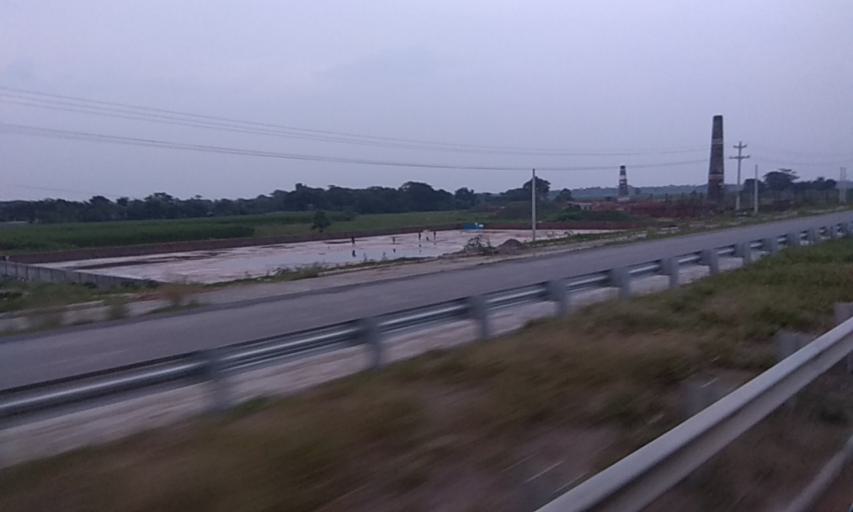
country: BD
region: Dhaka
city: Char Bhadrasan
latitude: 23.3704
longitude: 90.0425
